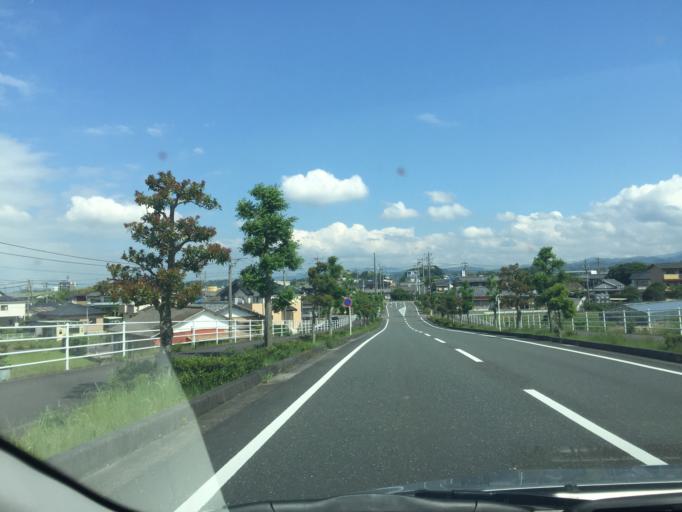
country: JP
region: Shizuoka
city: Kakegawa
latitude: 34.7696
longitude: 137.9948
